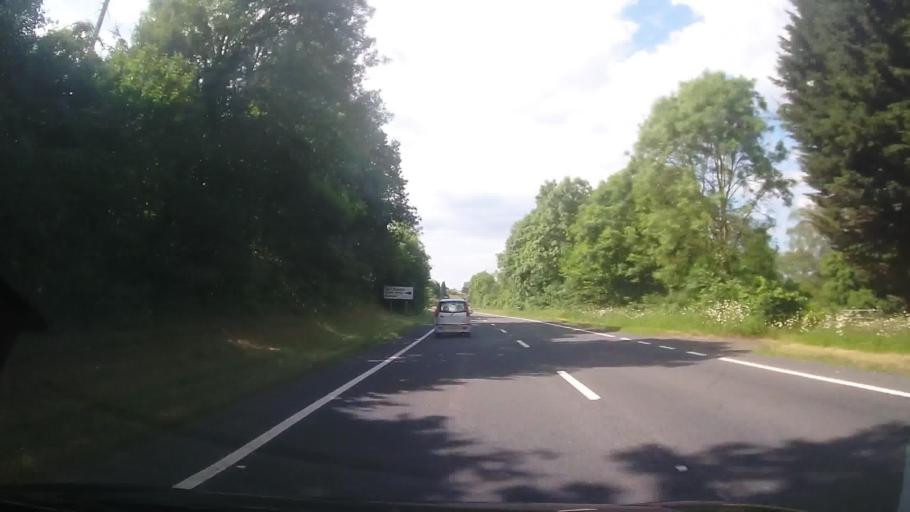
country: GB
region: England
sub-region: Herefordshire
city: Hope under Dinmore
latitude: 52.1885
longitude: -2.7168
